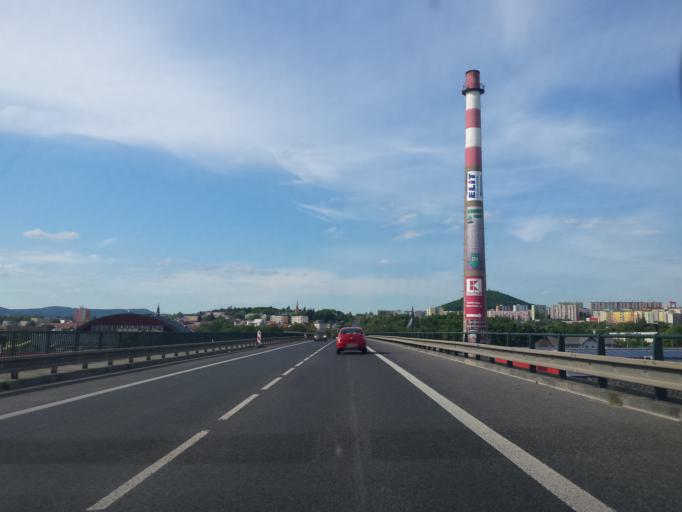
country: CZ
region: Liberecky
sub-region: Okres Ceska Lipa
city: Ceska Lipa
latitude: 50.6792
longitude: 14.5417
